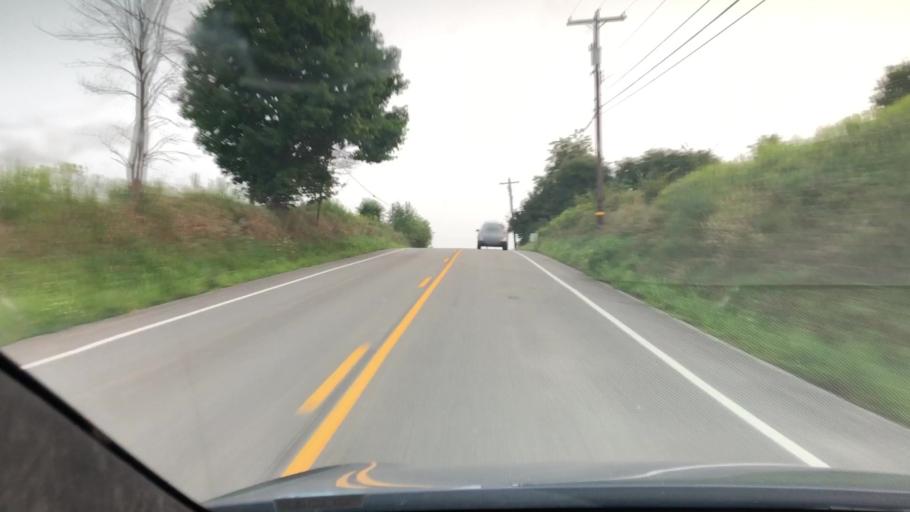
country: US
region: Pennsylvania
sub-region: Mercer County
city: Grove City
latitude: 41.1472
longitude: -80.0075
